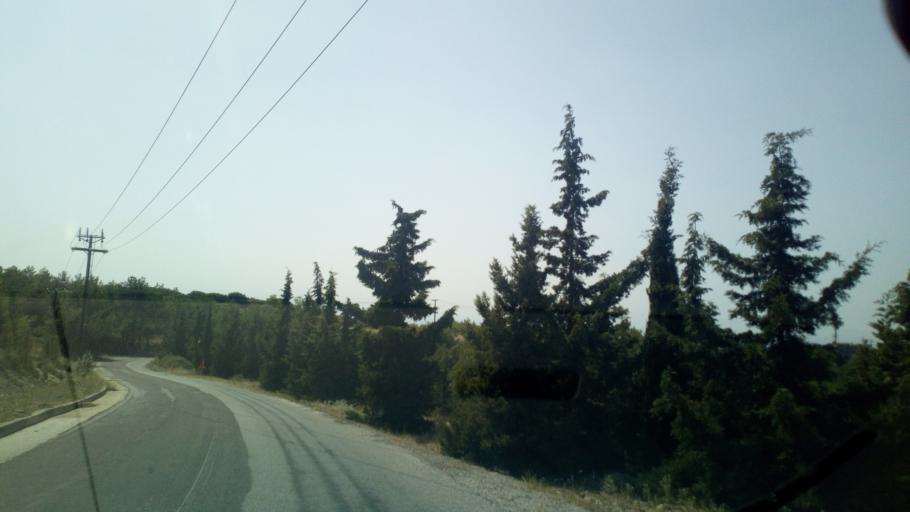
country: GR
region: Central Macedonia
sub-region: Nomos Thessalonikis
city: Pefka
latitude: 40.6434
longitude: 23.0003
